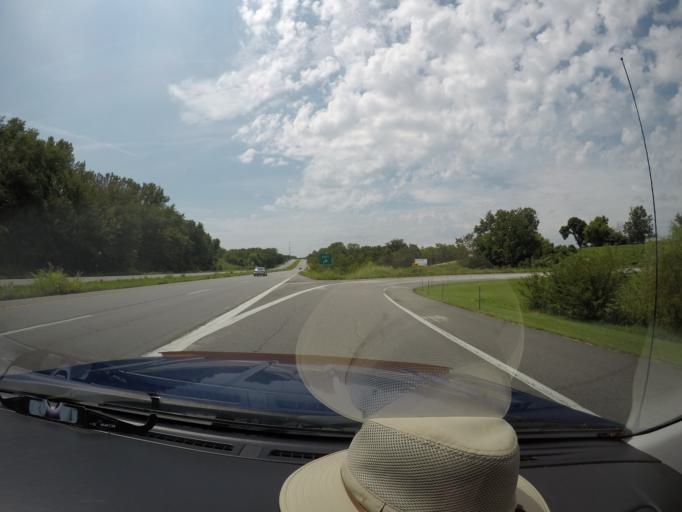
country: US
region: Missouri
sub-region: Lafayette County
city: Lexington
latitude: 39.1633
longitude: -93.8815
